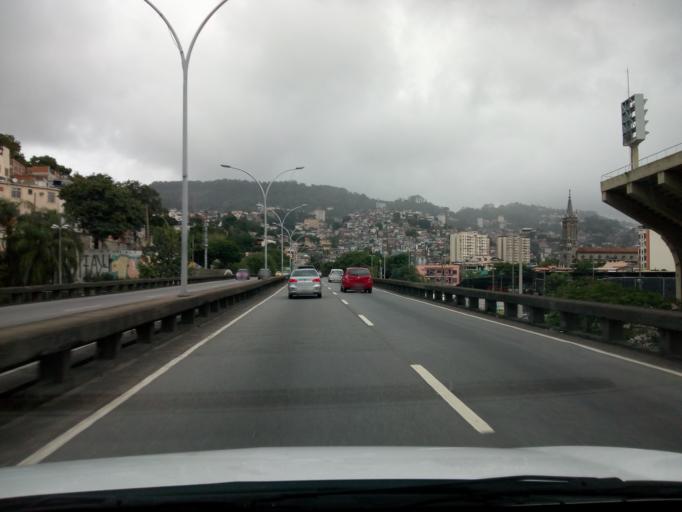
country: BR
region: Rio de Janeiro
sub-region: Rio De Janeiro
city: Rio de Janeiro
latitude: -22.9129
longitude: -43.1954
